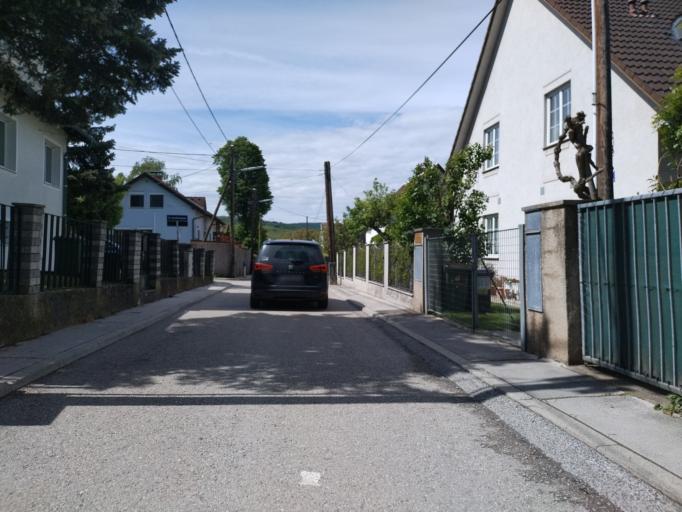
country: AT
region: Lower Austria
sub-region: Politischer Bezirk Wien-Umgebung
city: Purkersdorf
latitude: 48.2072
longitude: 16.2359
